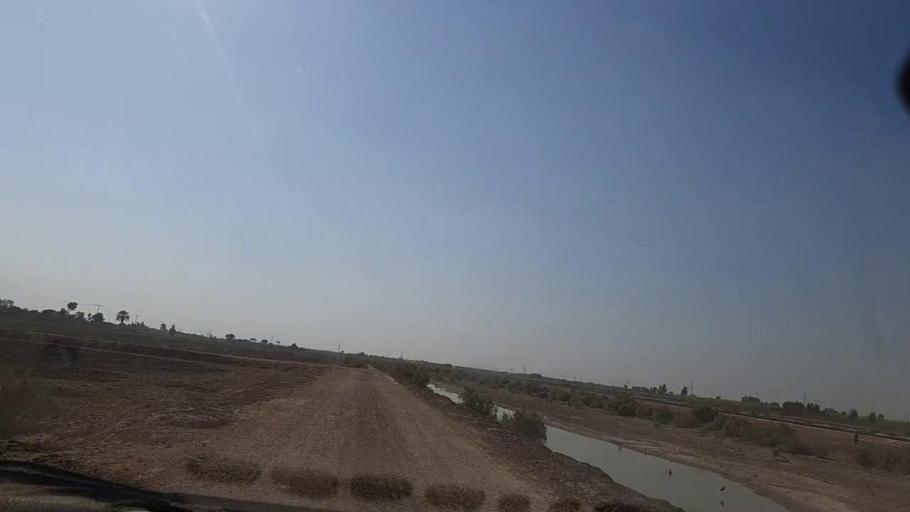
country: PK
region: Sindh
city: Mirpur Khas
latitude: 25.5087
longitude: 68.9102
